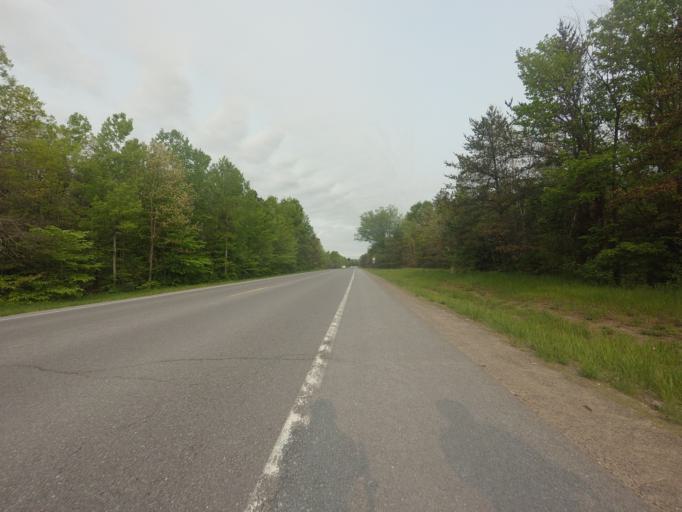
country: US
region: New York
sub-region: Jefferson County
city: Carthage
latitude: 44.0337
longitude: -75.6083
